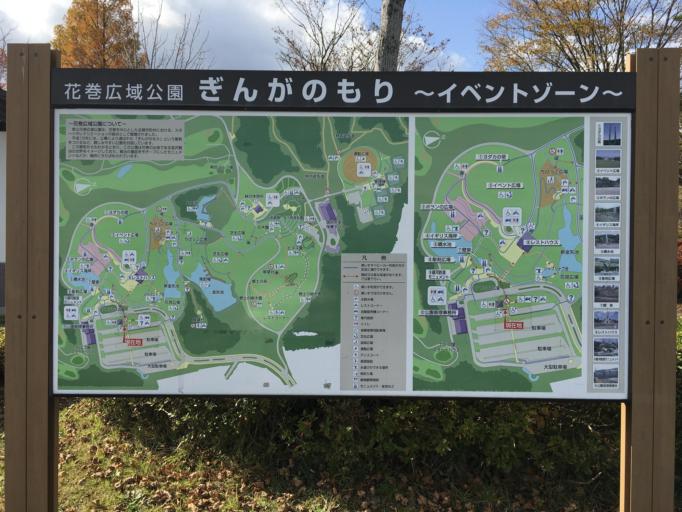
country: JP
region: Iwate
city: Hanamaki
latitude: 39.4324
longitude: 141.0582
